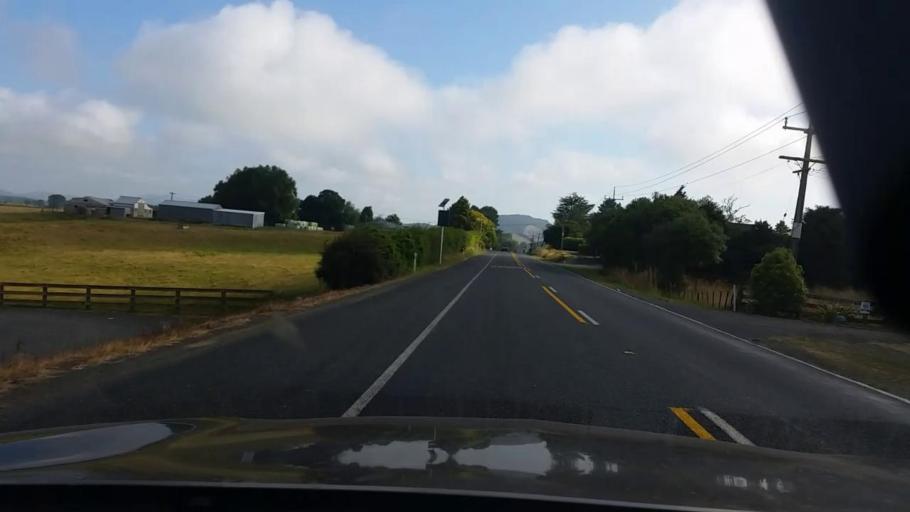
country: NZ
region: Waikato
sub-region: Hamilton City
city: Hamilton
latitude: -37.6135
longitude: 175.3450
